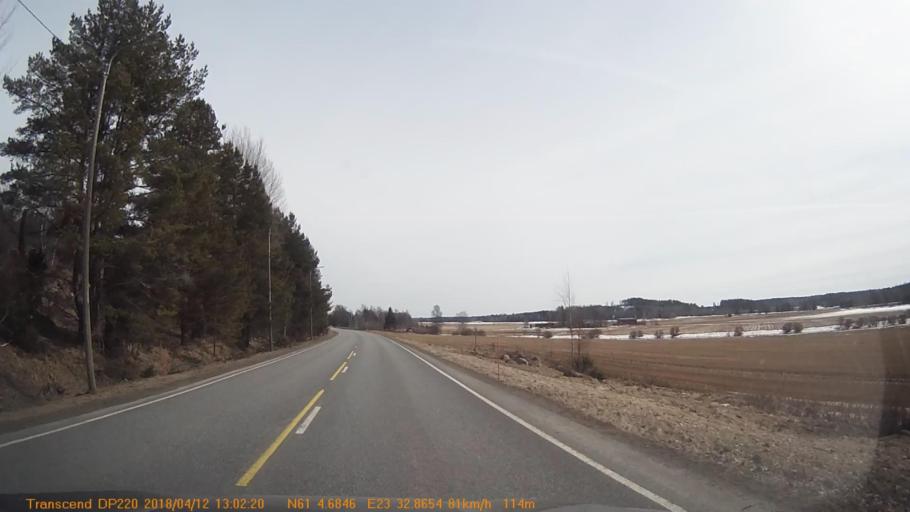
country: FI
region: Pirkanmaa
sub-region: Etelae-Pirkanmaa
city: Urjala
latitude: 61.0779
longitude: 23.5485
